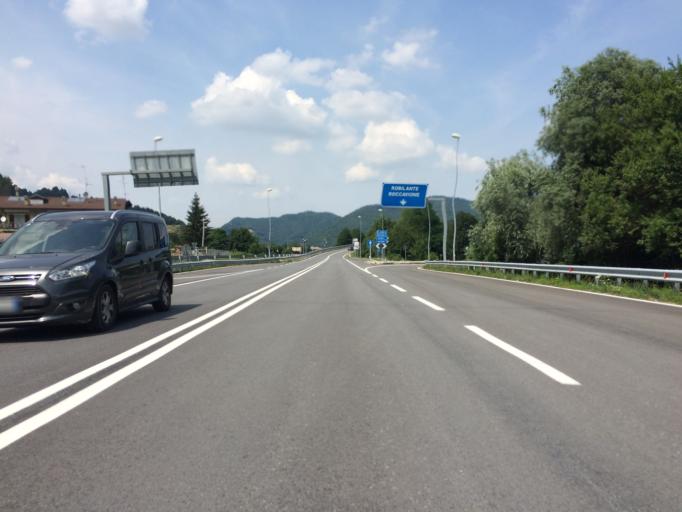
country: IT
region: Piedmont
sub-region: Provincia di Cuneo
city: Robilante
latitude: 44.2793
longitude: 7.5176
